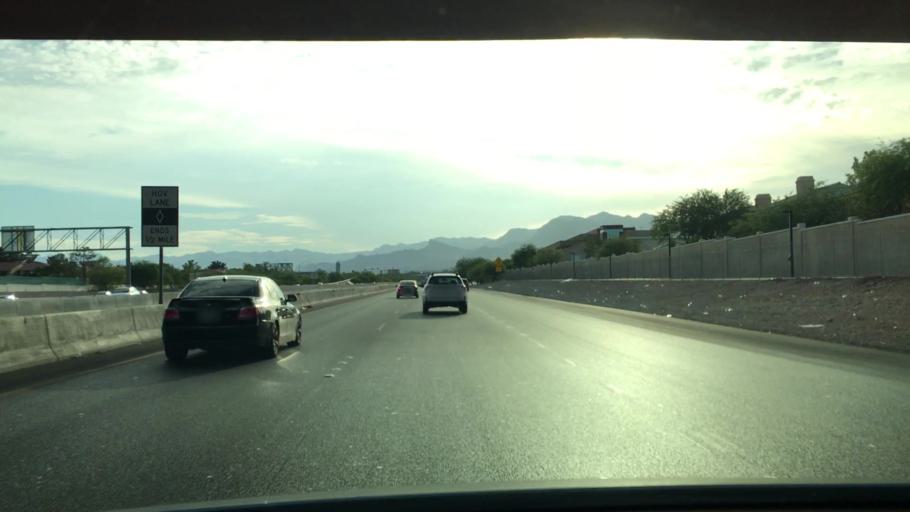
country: US
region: Nevada
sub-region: Clark County
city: Spring Valley
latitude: 36.1783
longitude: -115.2509
